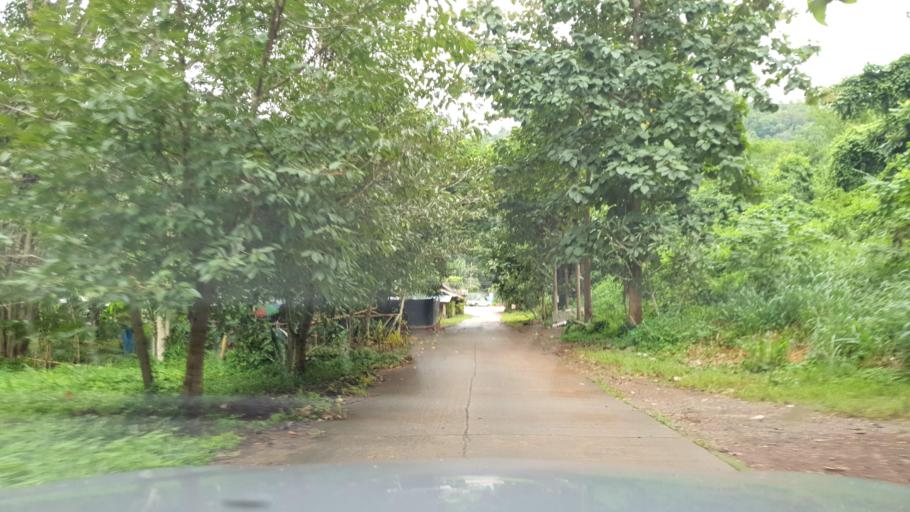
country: TH
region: Chiang Mai
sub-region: Amphoe Chiang Dao
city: Chiang Dao
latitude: 19.2842
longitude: 98.9672
